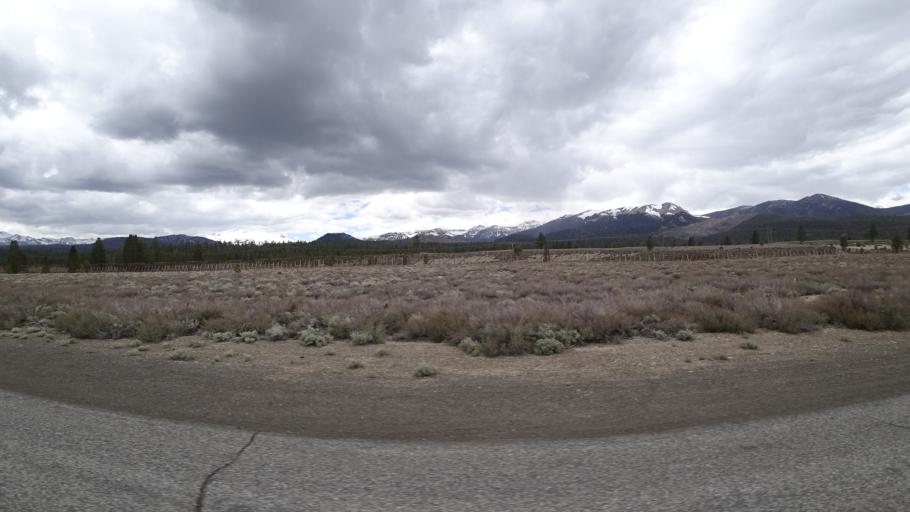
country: US
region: California
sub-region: Mono County
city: Mammoth Lakes
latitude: 37.7380
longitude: -118.9729
